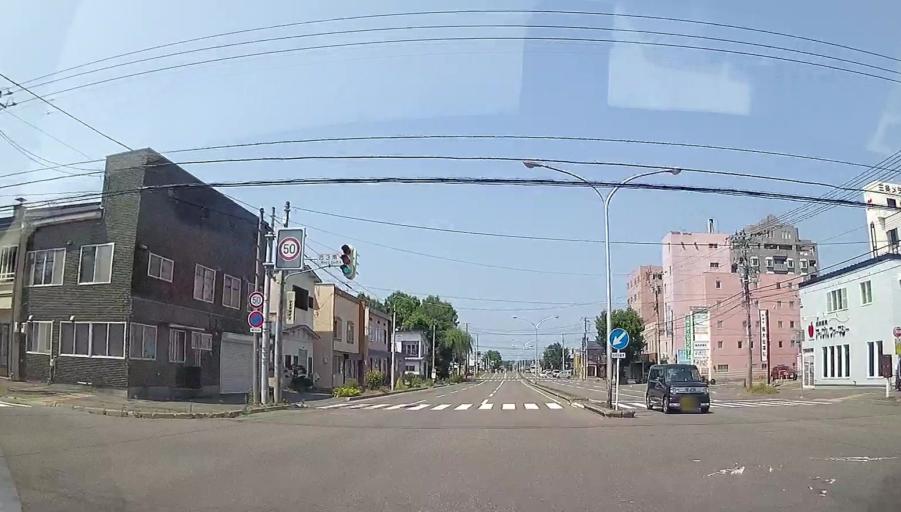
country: JP
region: Hokkaido
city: Obihiro
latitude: 42.9269
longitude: 143.1998
